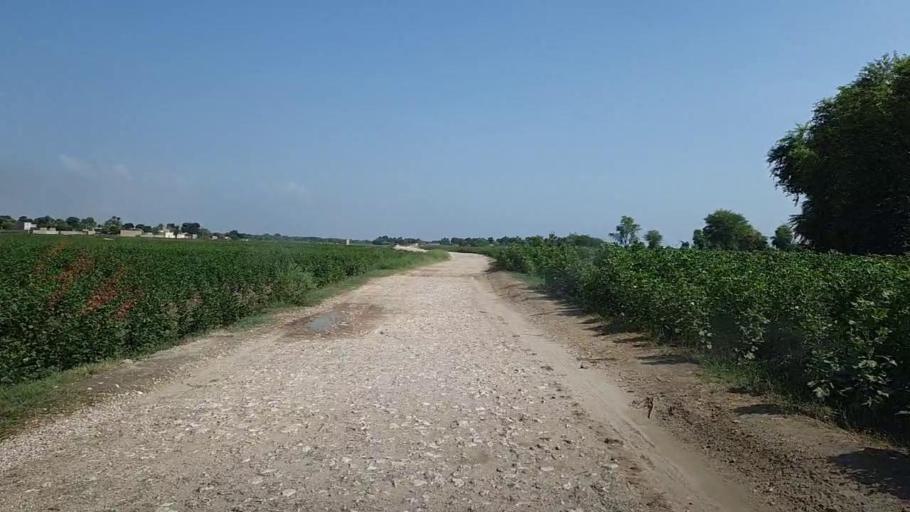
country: PK
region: Sindh
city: Bhiria
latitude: 26.8756
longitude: 68.2311
